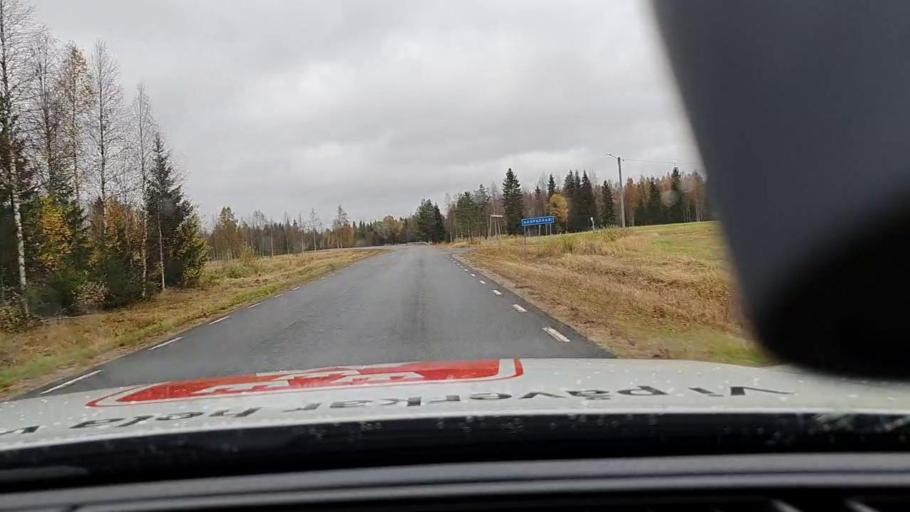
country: SE
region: Norrbotten
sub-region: Haparanda Kommun
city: Haparanda
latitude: 65.9319
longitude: 23.8156
